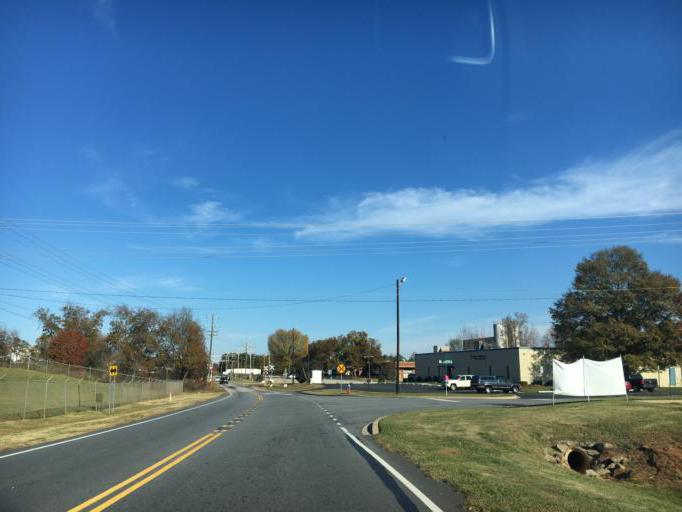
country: US
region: South Carolina
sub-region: Spartanburg County
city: Southern Shops
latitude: 35.0035
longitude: -82.0371
